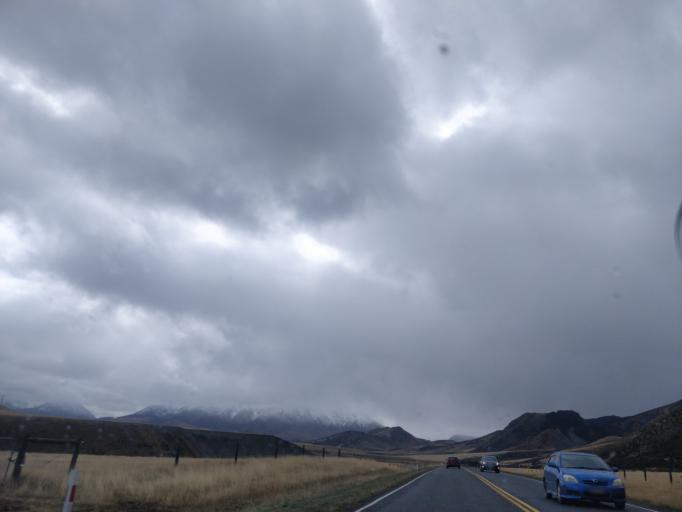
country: NZ
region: Canterbury
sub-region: Ashburton District
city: Methven
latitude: -43.2499
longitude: 171.7180
